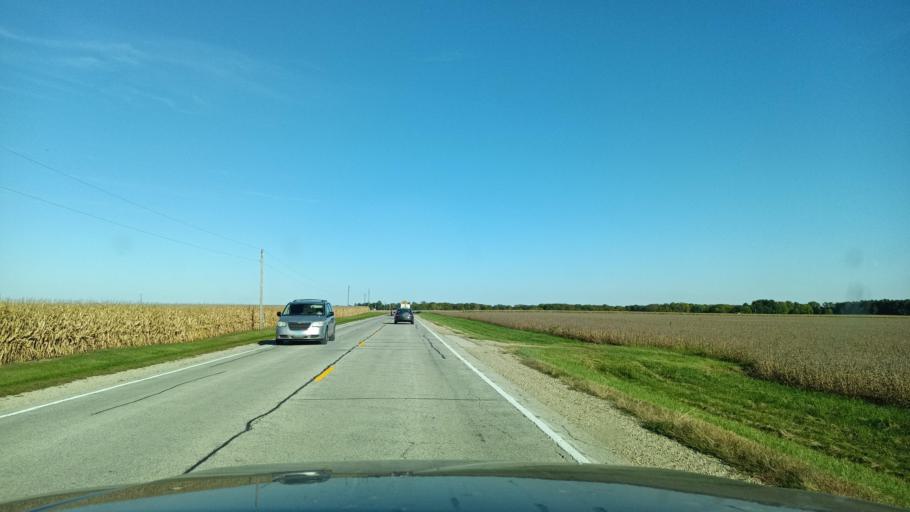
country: US
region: Illinois
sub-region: De Witt County
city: Farmer City
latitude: 40.2239
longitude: -88.7120
